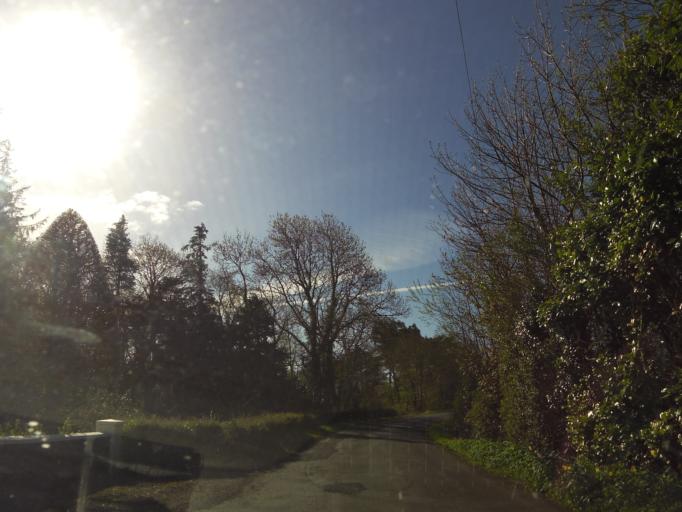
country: IE
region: Connaught
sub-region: Maigh Eo
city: Kiltamagh
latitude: 53.7849
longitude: -8.9613
